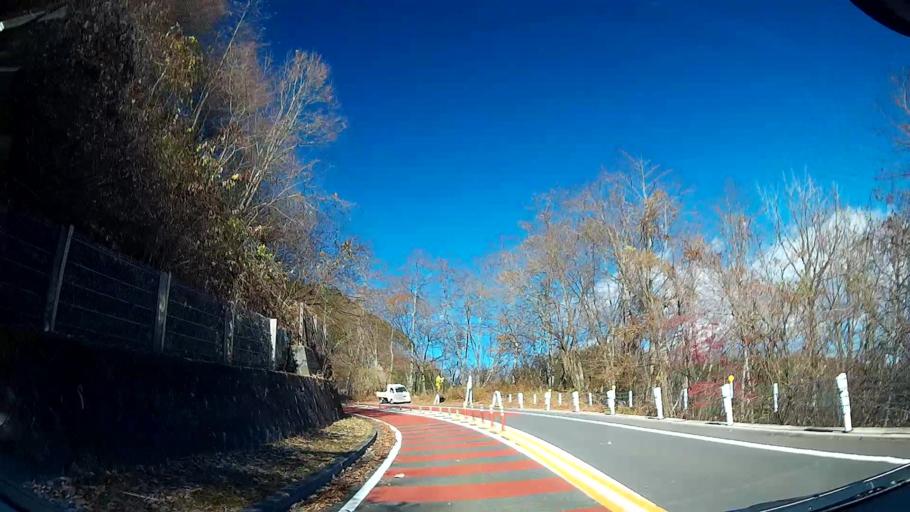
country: JP
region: Yamanashi
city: Uenohara
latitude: 35.7433
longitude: 139.0436
